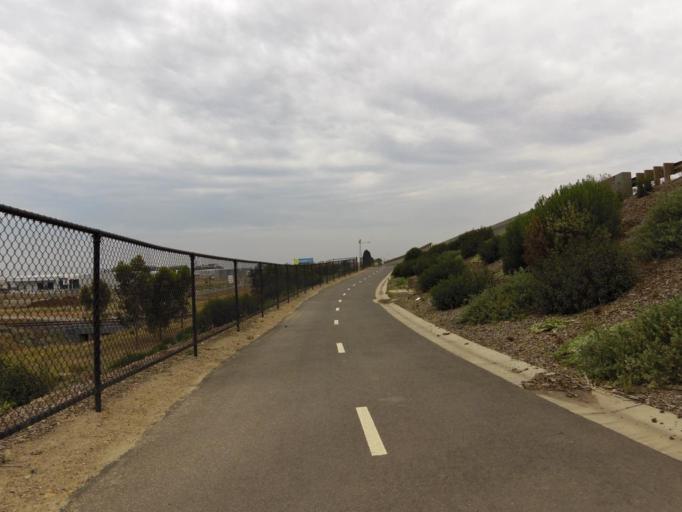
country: AU
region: Victoria
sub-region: Brimbank
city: Derrimut
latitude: -37.7722
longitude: 144.7465
